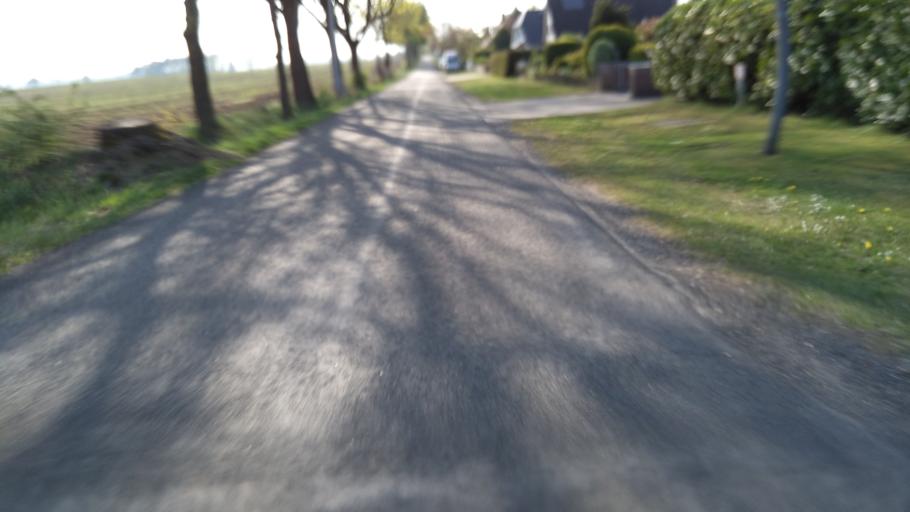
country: DE
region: Lower Saxony
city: Buxtehude
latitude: 53.4364
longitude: 9.6909
